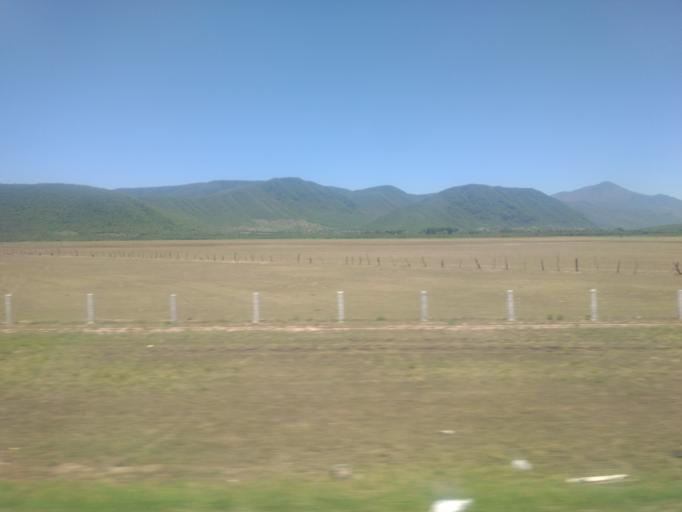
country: MX
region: Jalisco
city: Zacoalco de Torres
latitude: 20.1643
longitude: -103.5025
